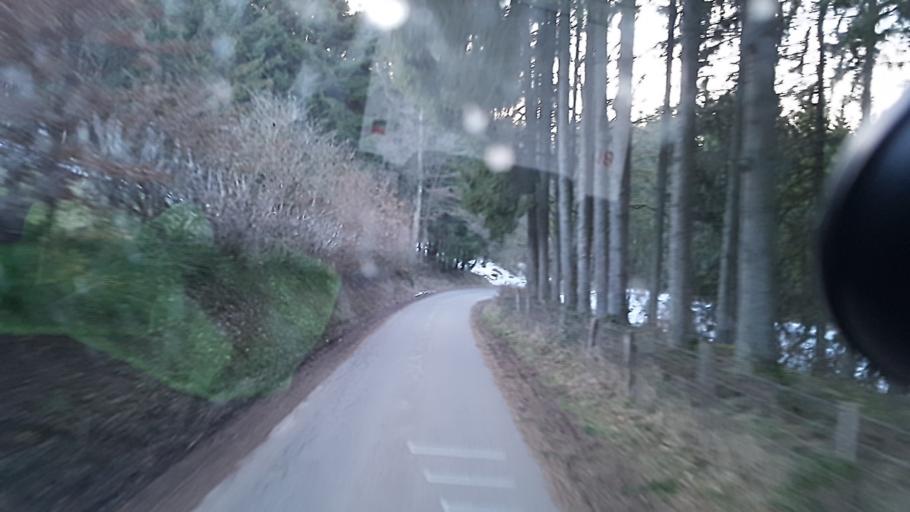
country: BE
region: Wallonia
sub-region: Province du Luxembourg
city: Daverdisse
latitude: 50.0091
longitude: 5.1379
